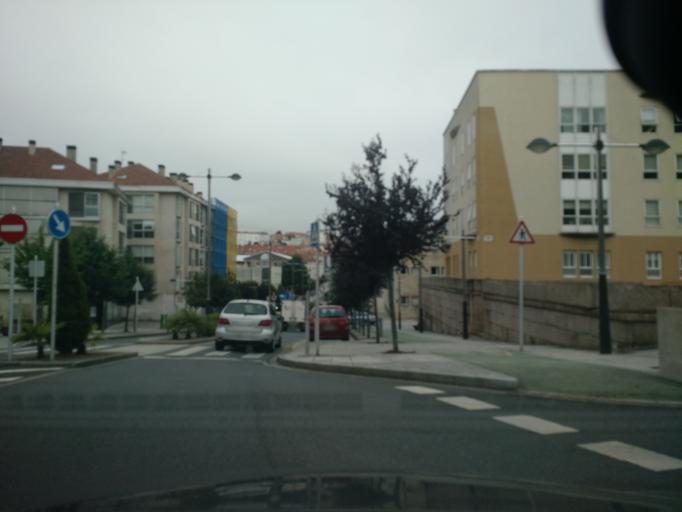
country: ES
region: Galicia
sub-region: Provincia da Coruna
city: Santiago de Compostela
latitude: 42.8804
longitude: -8.5267
